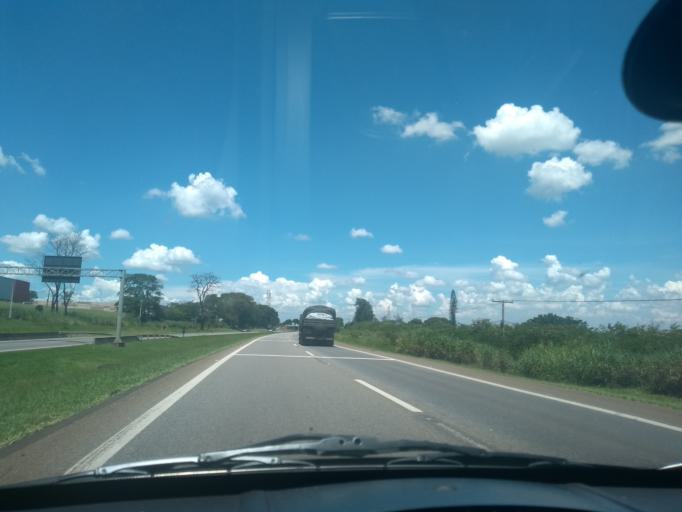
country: BR
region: Sao Paulo
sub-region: Mogi-Mirim
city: Mogi Mirim
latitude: -22.4867
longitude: -46.9812
